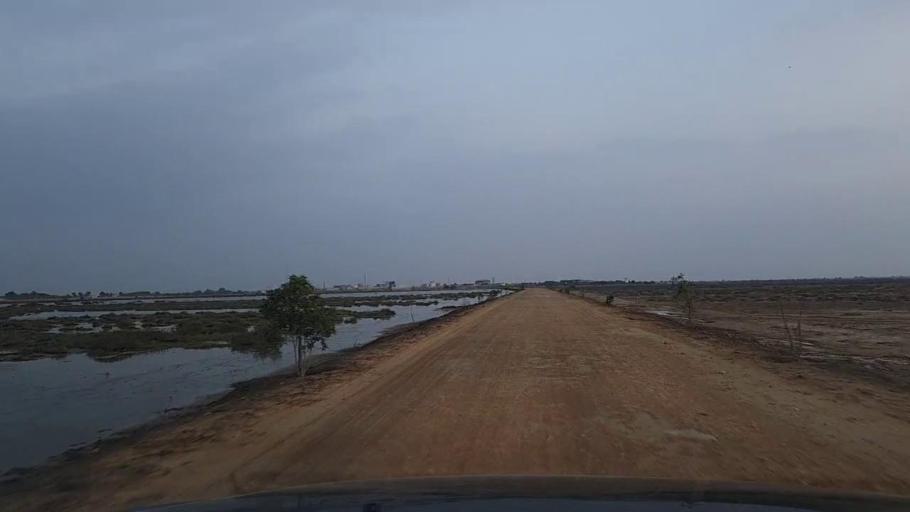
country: PK
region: Sindh
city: Jati
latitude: 24.4948
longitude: 68.3873
